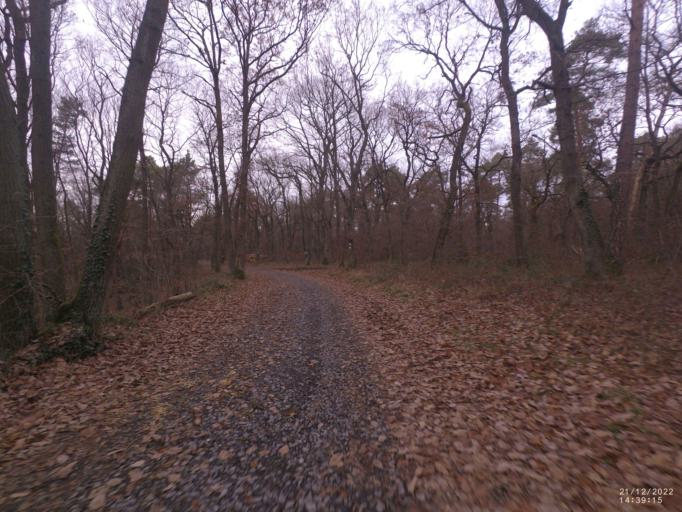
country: DE
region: Rheinland-Pfalz
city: Sinzig
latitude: 50.5273
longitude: 7.2612
